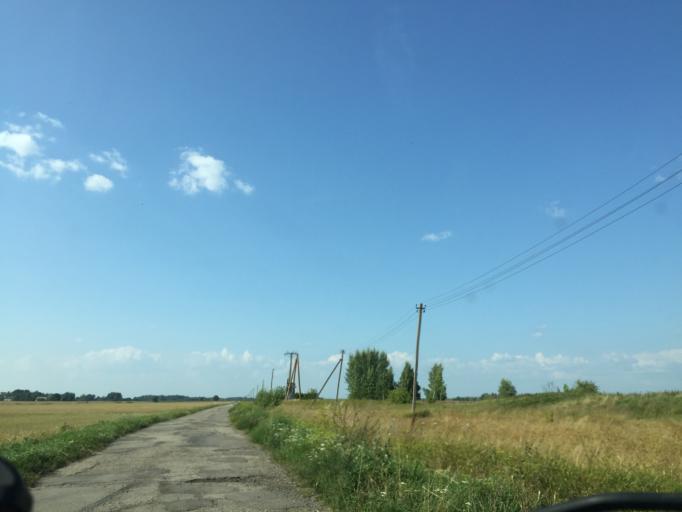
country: LV
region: Jelgava
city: Jelgava
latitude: 56.4547
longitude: 23.6810
